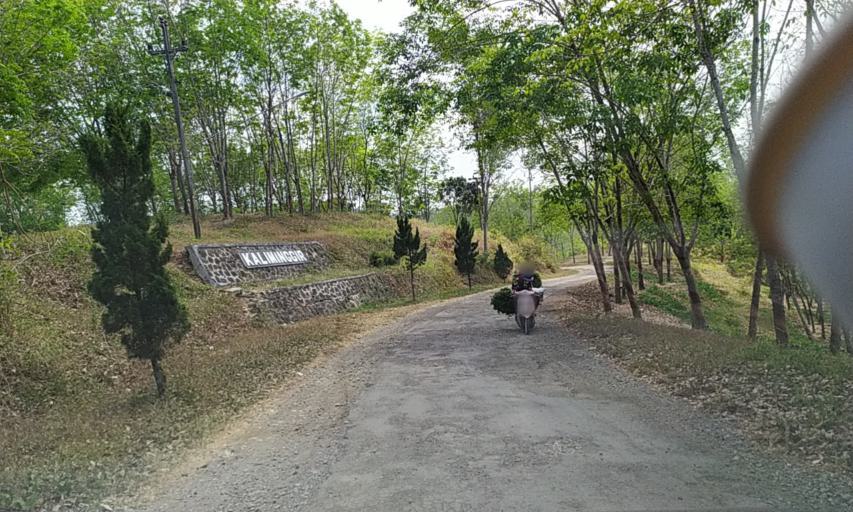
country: ID
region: Central Java
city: Prapagan
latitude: -7.5600
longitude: 109.0143
